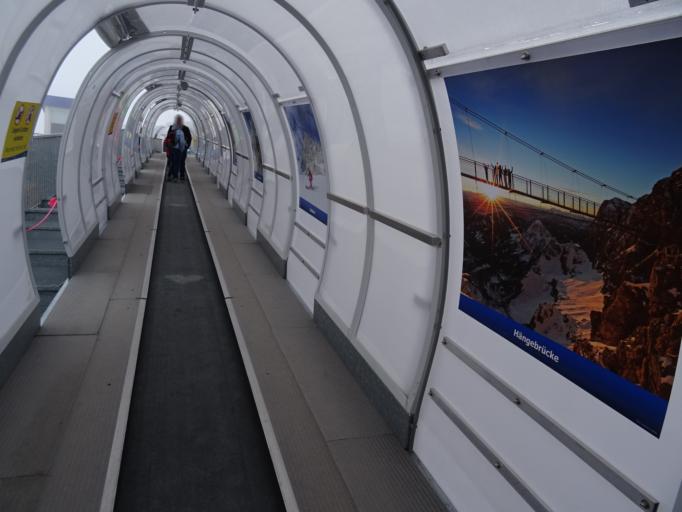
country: AT
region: Styria
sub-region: Politischer Bezirk Liezen
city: Schladming
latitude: 47.4688
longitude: 13.6257
